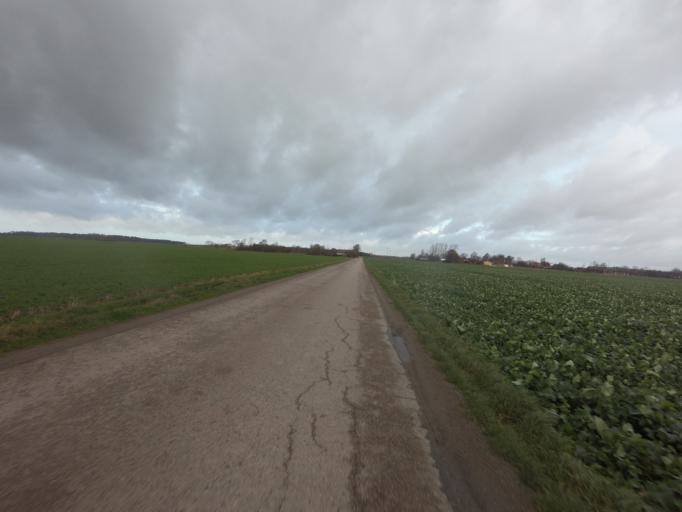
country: SE
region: Skane
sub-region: Helsingborg
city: Odakra
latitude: 56.1361
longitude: 12.7653
